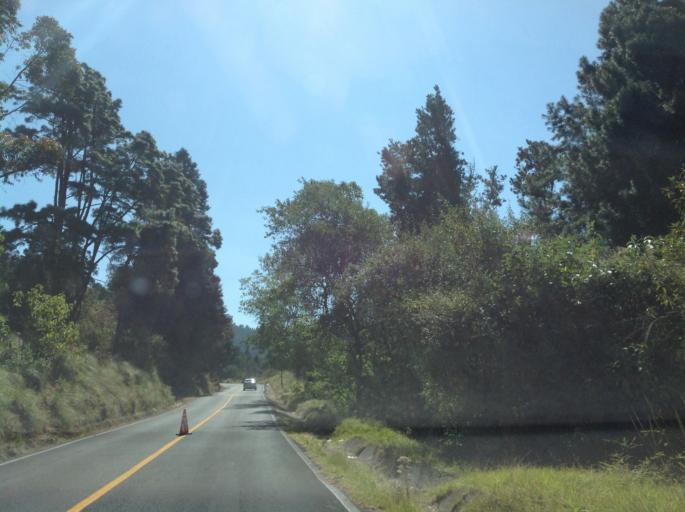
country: MX
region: Mexico
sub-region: Amecameca
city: San Diego Huehuecalco
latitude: 19.0722
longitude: -98.7008
